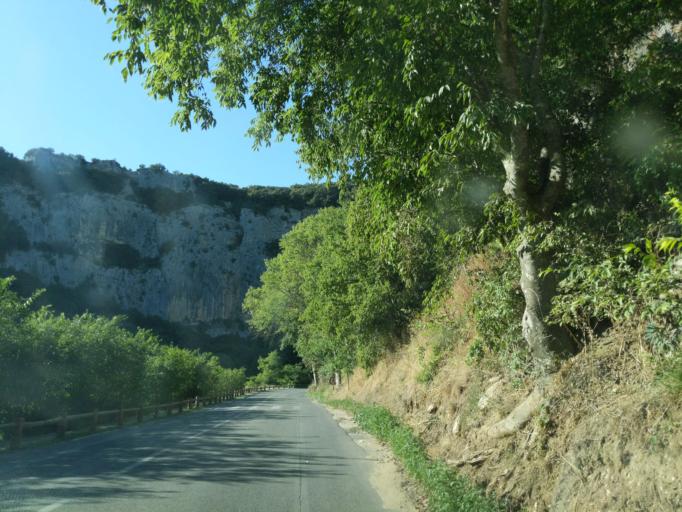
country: FR
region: Rhone-Alpes
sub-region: Departement de l'Ardeche
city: Ruoms
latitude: 44.3848
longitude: 4.4139
